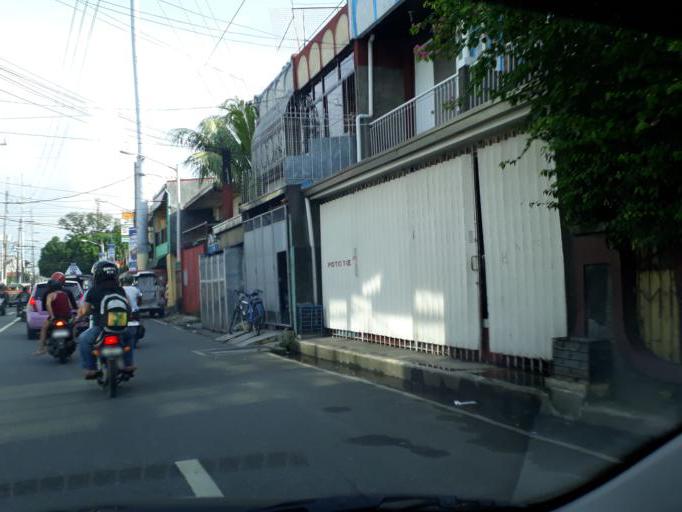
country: PH
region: Metro Manila
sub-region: Caloocan City
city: Niugan
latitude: 14.6472
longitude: 120.9737
